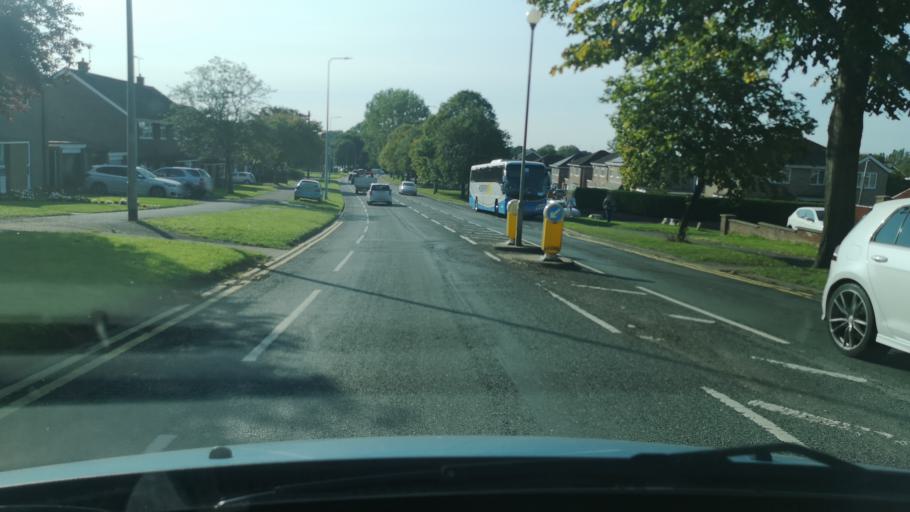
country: GB
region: England
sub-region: North Lincolnshire
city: Scunthorpe
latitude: 53.5745
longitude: -0.6729
